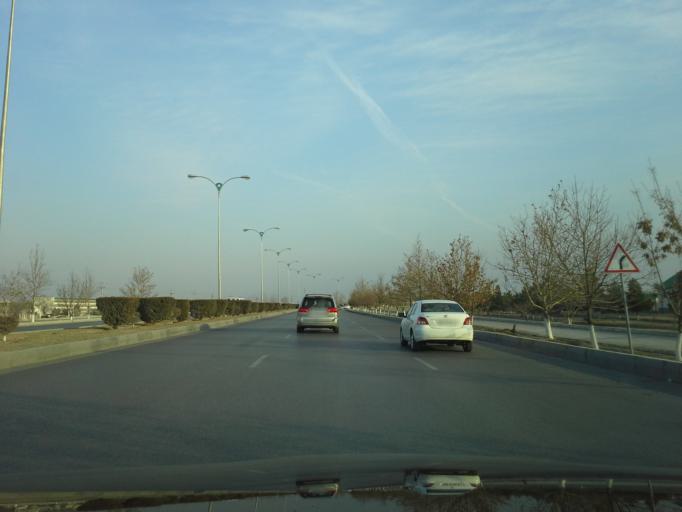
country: TM
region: Ahal
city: Abadan
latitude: 38.0569
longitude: 58.1793
